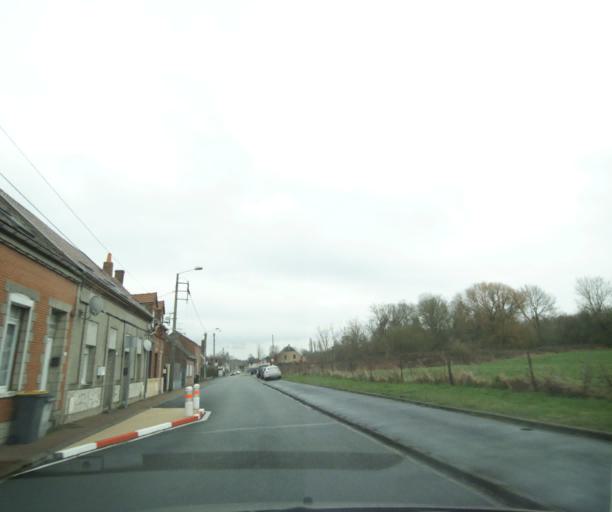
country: FR
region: Nord-Pas-de-Calais
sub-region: Departement du Nord
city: Haulchin
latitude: 50.3235
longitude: 3.4418
